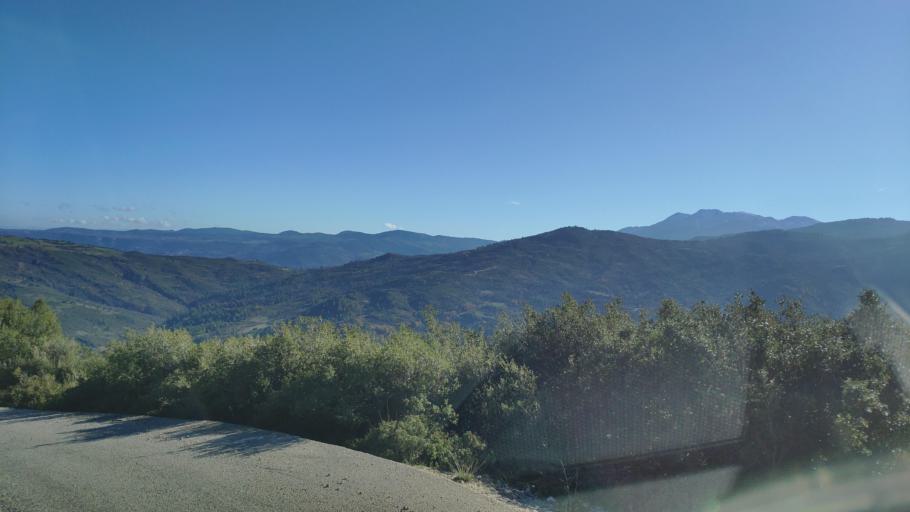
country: GR
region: West Greece
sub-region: Nomos Achaias
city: Aiyira
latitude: 38.0599
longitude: 22.4512
